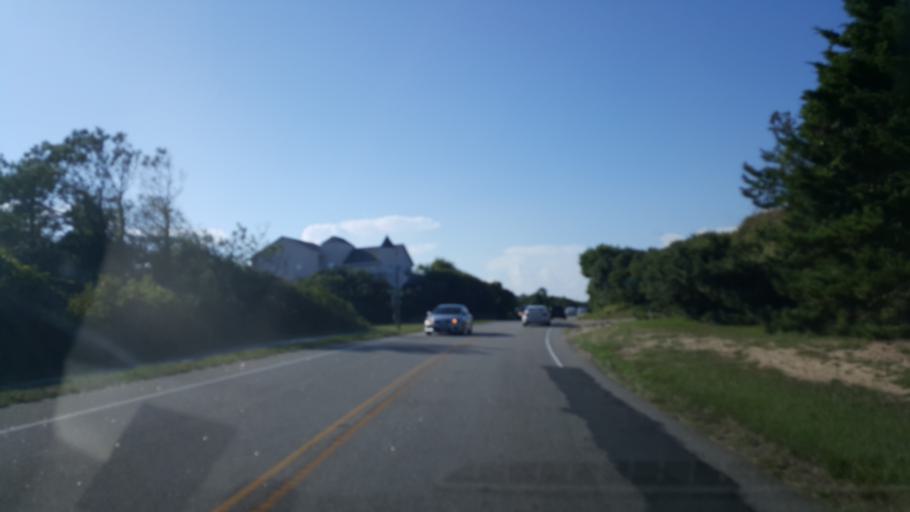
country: US
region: North Carolina
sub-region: Dare County
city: Southern Shores
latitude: 36.1219
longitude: -75.7255
